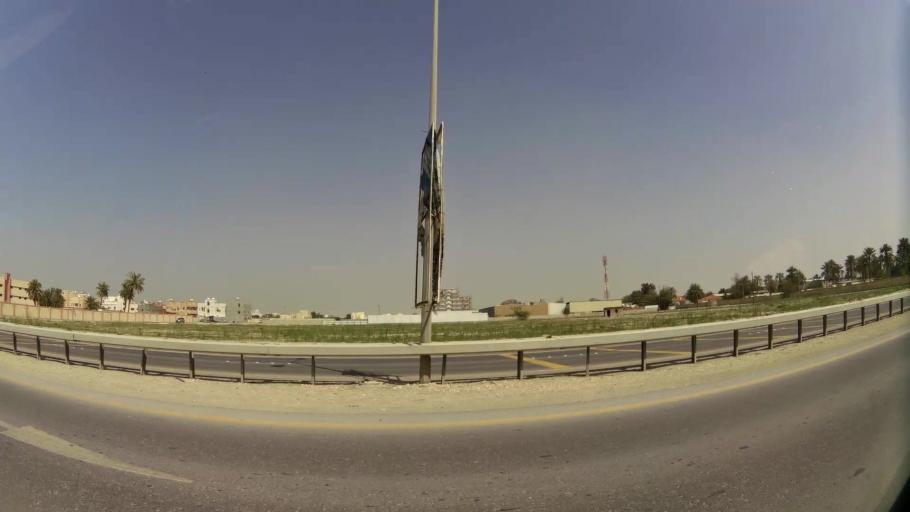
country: BH
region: Manama
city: Jidd Hafs
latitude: 26.2044
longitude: 50.4586
